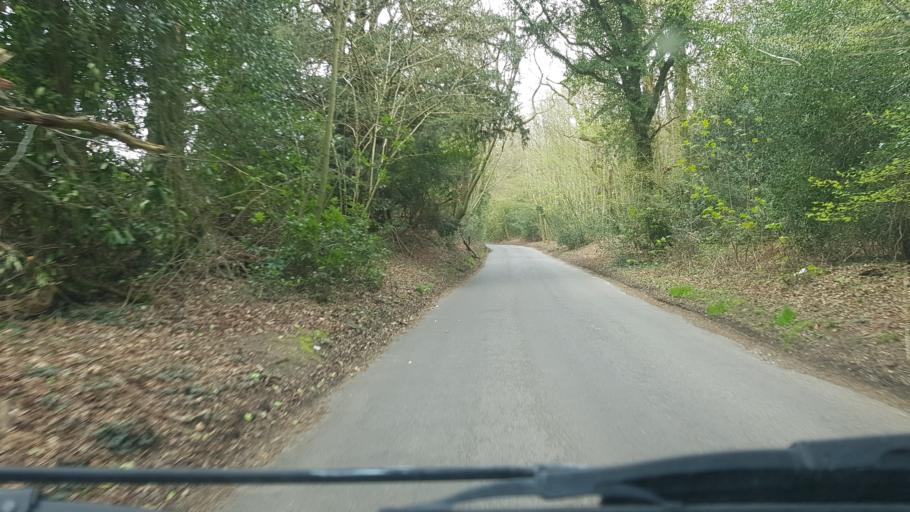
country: GB
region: England
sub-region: Surrey
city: Cranleigh
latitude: 51.1668
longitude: -0.4505
